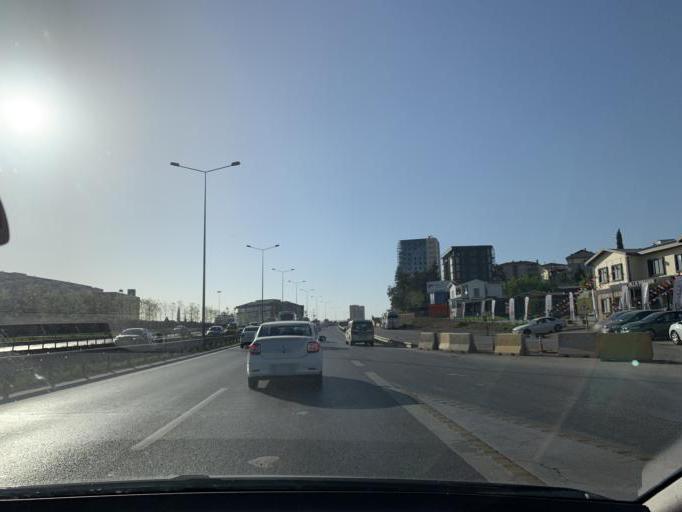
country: TR
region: Istanbul
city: Icmeler
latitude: 40.8447
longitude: 29.3051
